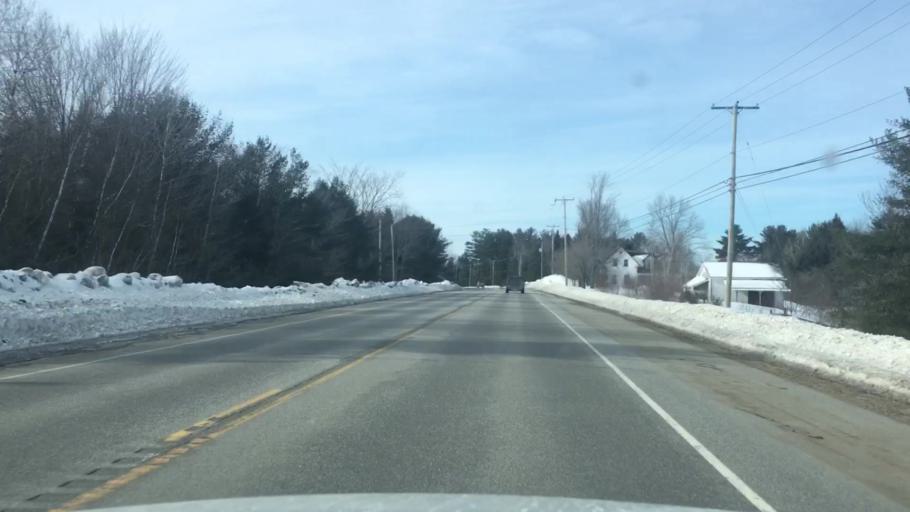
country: US
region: Maine
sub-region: Penobscot County
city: Kenduskeag
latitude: 44.9572
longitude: -68.9529
